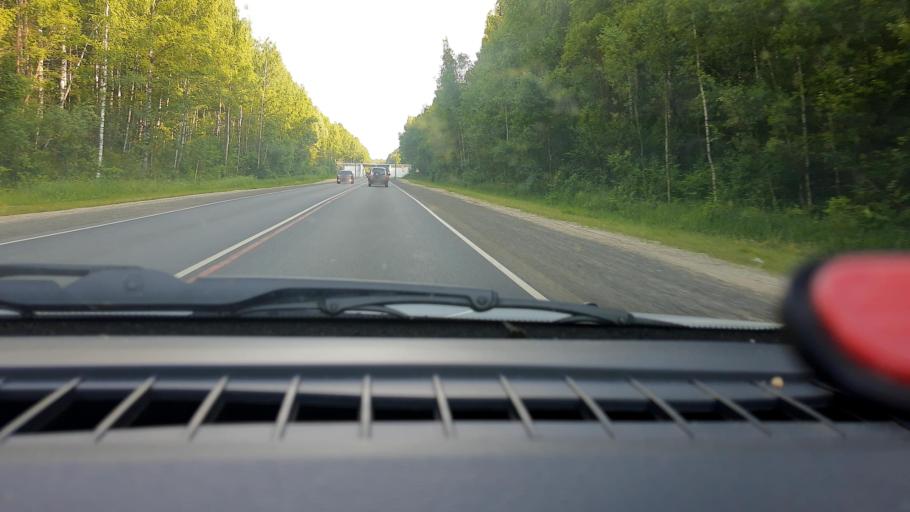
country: RU
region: Nizjnij Novgorod
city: Arzamas
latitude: 55.4341
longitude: 43.8983
